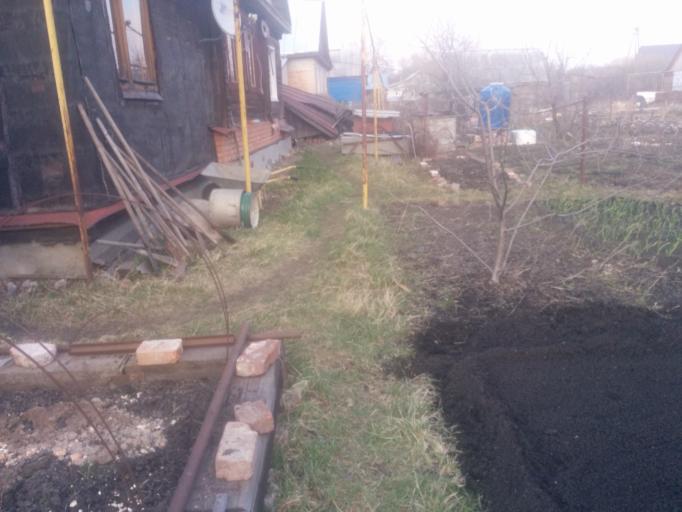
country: RU
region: Penza
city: Penza
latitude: 53.2006
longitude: 45.0600
